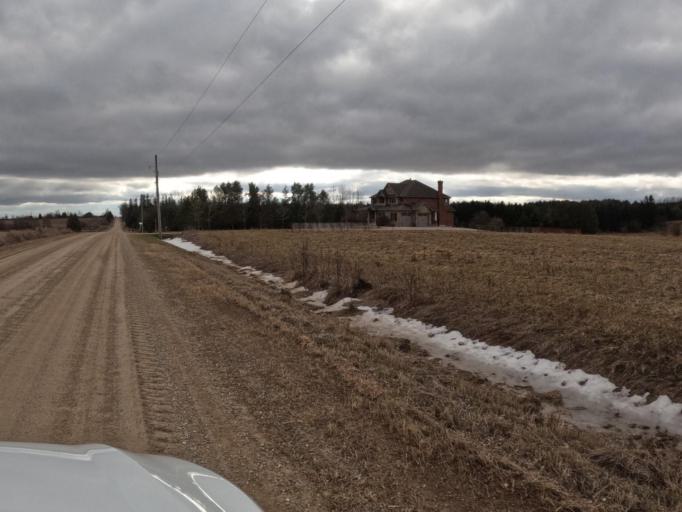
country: CA
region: Ontario
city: Shelburne
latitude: 43.8801
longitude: -80.3808
